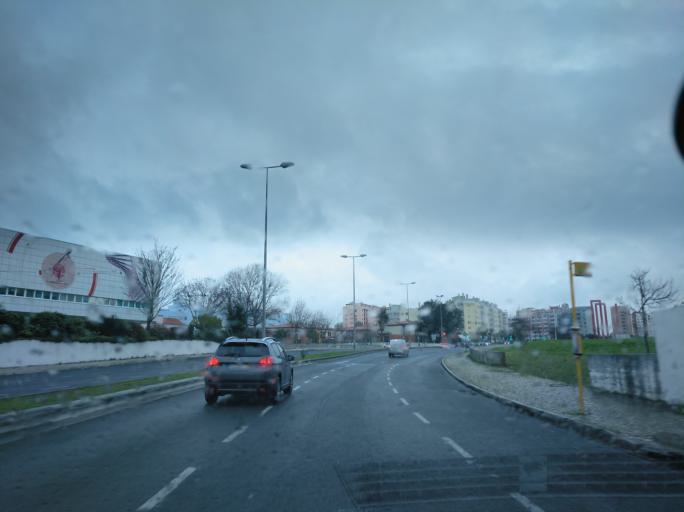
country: PT
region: Lisbon
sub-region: Odivelas
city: Pontinha
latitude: 38.7666
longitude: -9.1843
